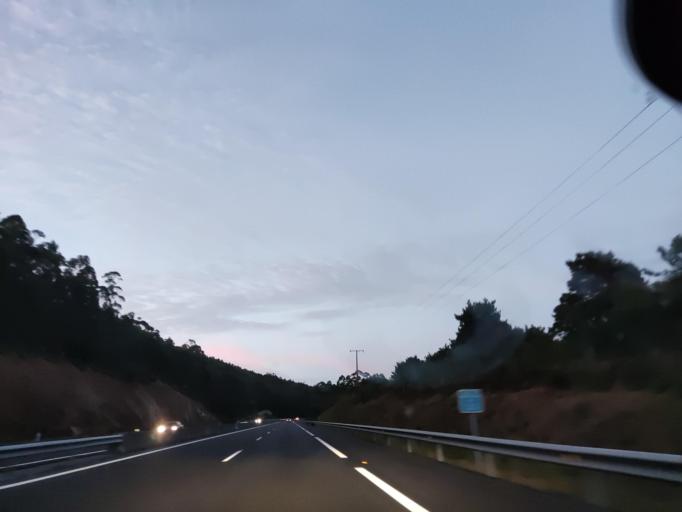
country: ES
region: Galicia
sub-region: Provincia da Coruna
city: Boiro
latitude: 42.6163
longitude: -8.9530
